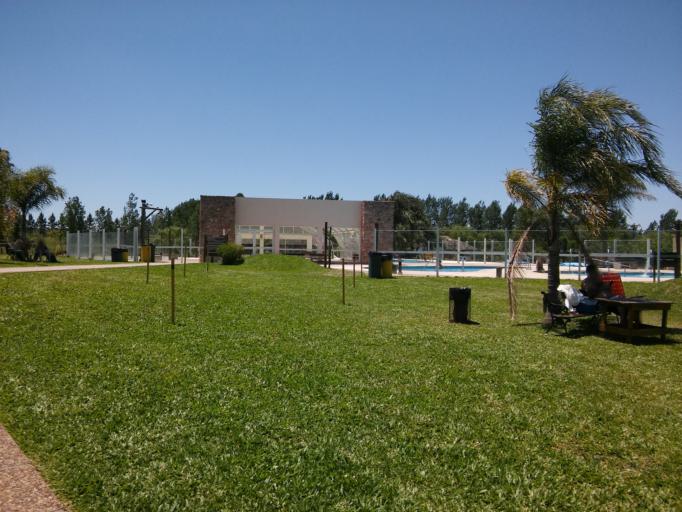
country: AR
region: Entre Rios
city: Concepcion del Uruguay
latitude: -32.4515
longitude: -58.2917
